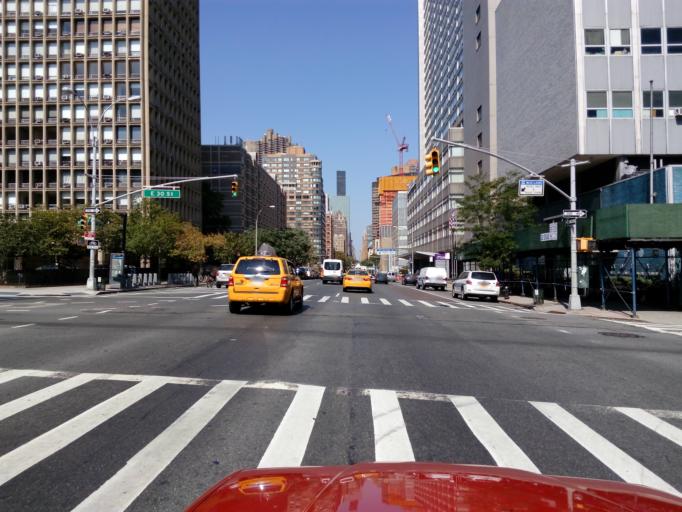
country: US
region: New York
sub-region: Queens County
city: Long Island City
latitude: 40.7411
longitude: -73.9754
